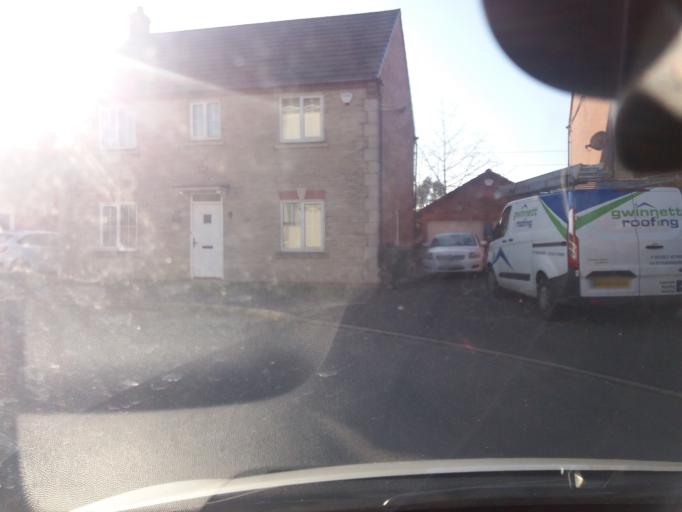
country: GB
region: England
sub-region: Lancashire
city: Adlington
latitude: 53.6206
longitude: -2.6083
